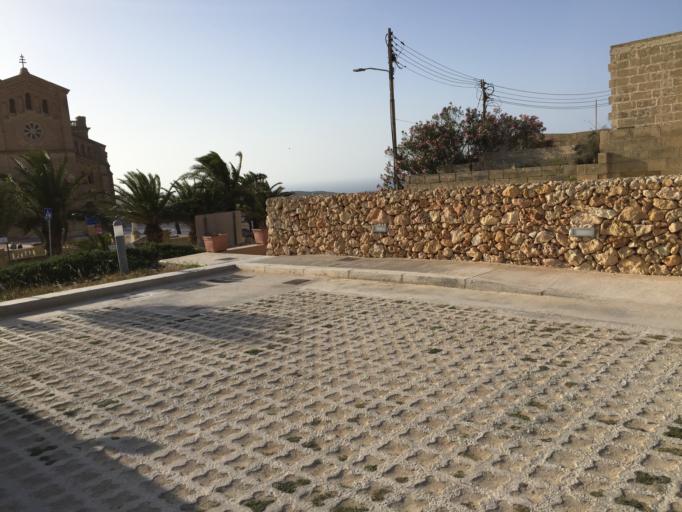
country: MT
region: L-Gharb
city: Gharb
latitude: 36.0611
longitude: 14.2162
